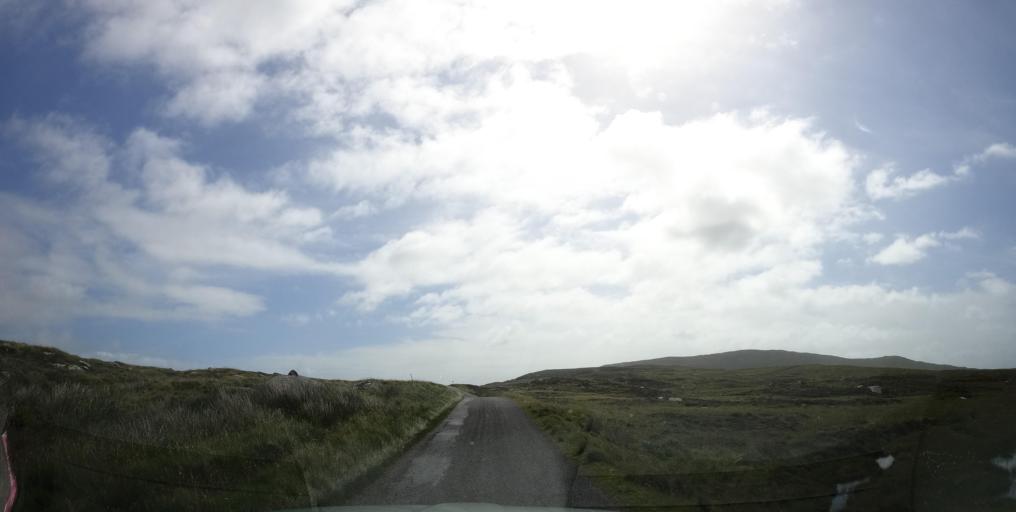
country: GB
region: Scotland
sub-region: Eilean Siar
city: Isle of South Uist
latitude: 57.1385
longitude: -7.3571
